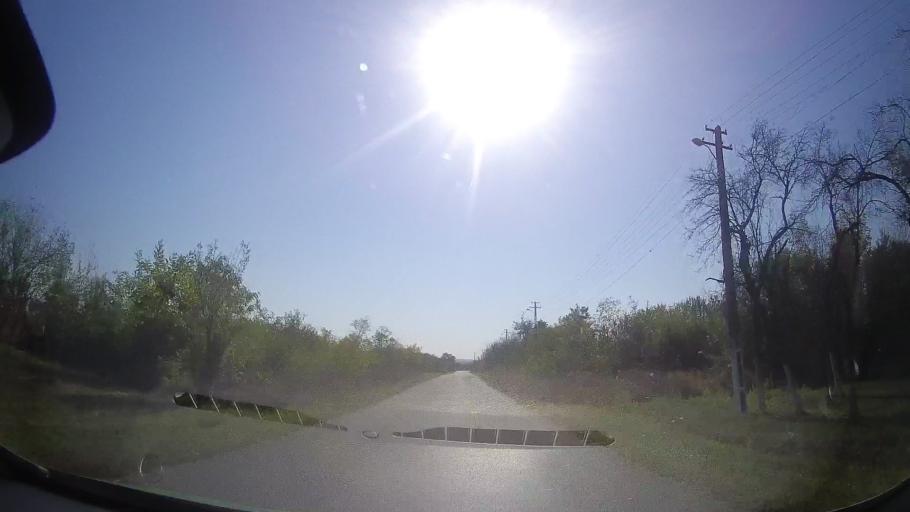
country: RO
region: Timis
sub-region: Comuna Ghizela
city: Ghizela
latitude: 45.8268
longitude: 21.7503
